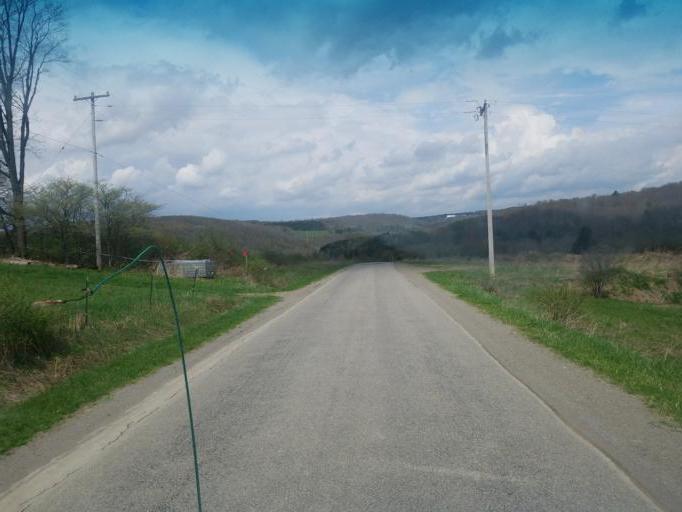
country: US
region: New York
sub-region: Allegany County
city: Andover
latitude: 42.0327
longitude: -77.7607
